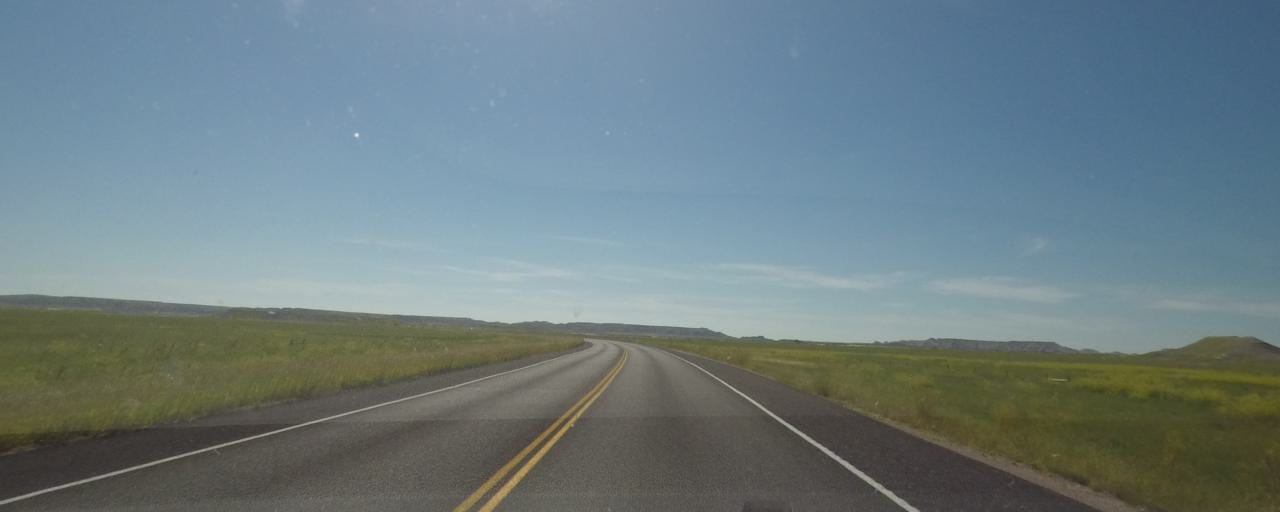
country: US
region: South Dakota
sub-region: Shannon County
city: Porcupine
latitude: 43.7798
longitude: -102.5491
